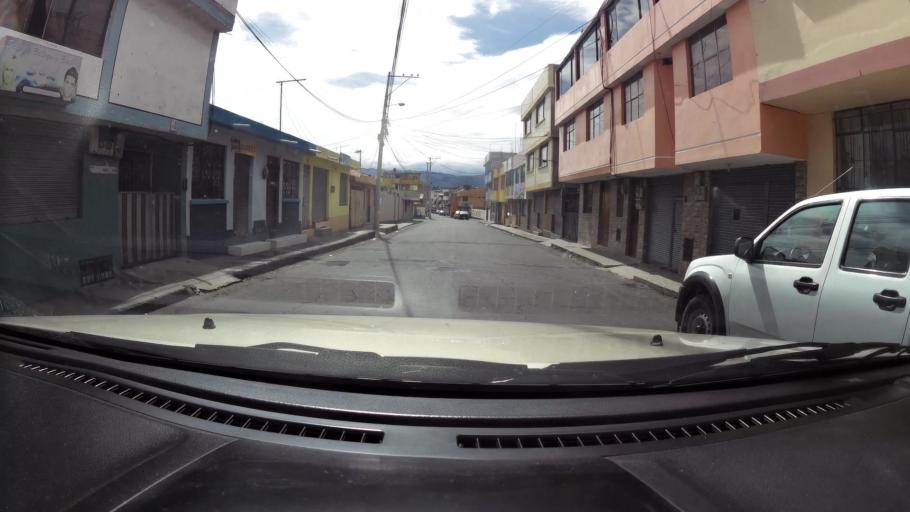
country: EC
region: Cotopaxi
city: Latacunga
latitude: -0.9307
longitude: -78.6217
